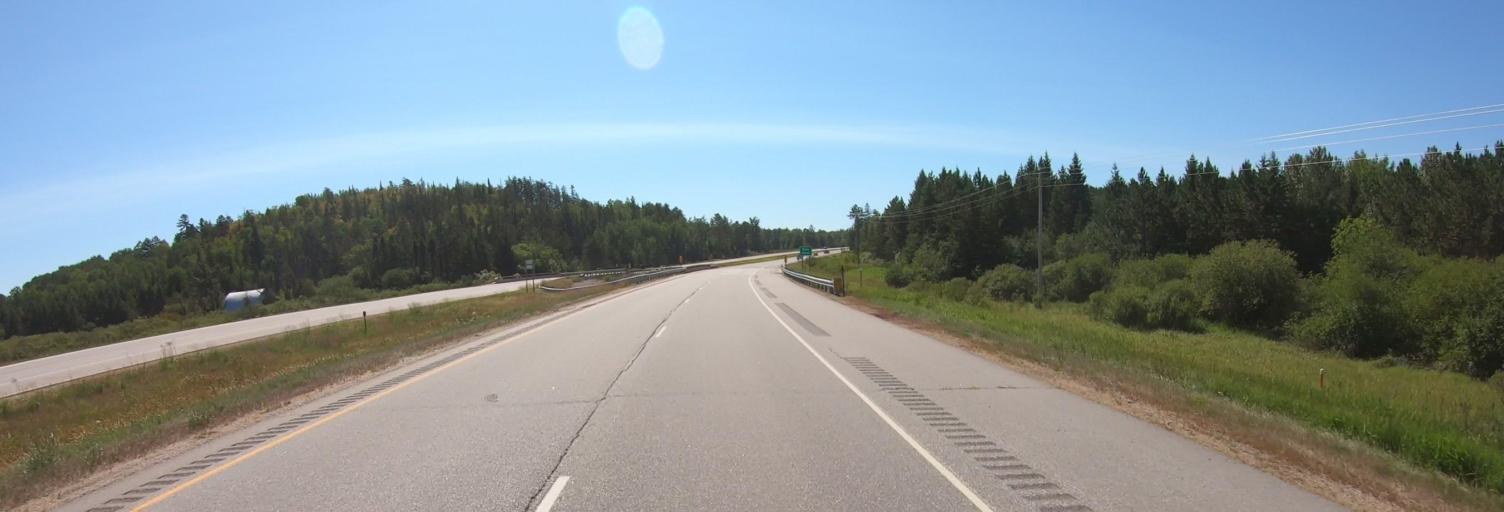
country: US
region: Minnesota
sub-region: Saint Louis County
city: Mountain Iron
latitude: 47.7081
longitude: -92.6465
